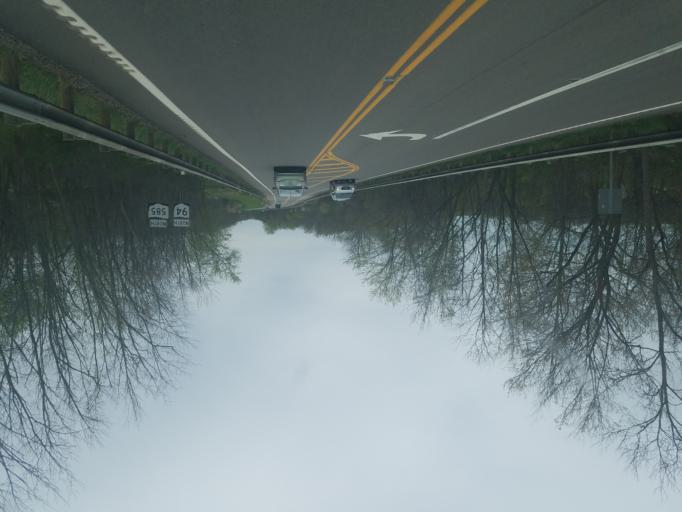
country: US
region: Ohio
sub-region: Wayne County
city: Rittman
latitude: 40.9453
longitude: -81.7439
